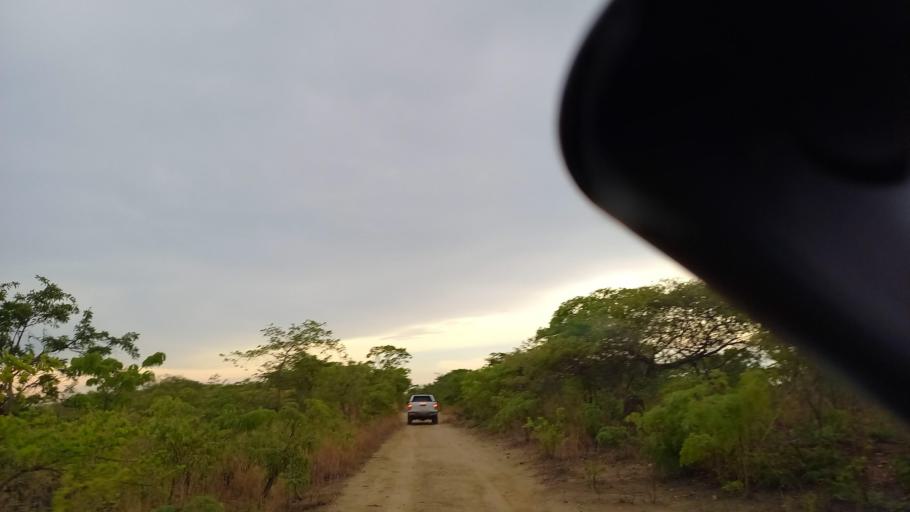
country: ZM
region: Lusaka
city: Kafue
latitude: -16.0481
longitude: 28.3279
